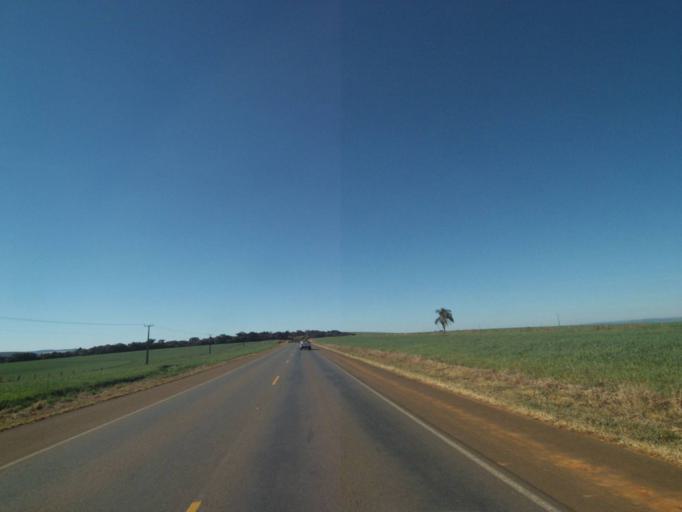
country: BR
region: Parana
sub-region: Tibagi
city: Tibagi
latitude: -24.4297
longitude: -50.4062
